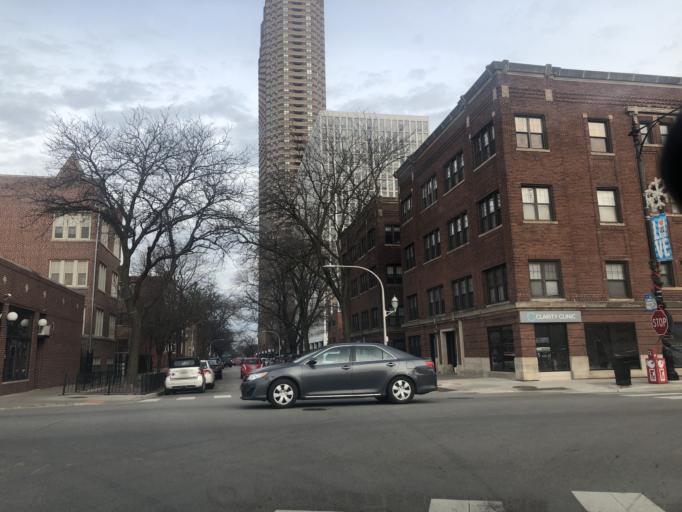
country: US
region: Illinois
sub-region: Cook County
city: Lincolnwood
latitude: 41.9491
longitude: -87.6485
